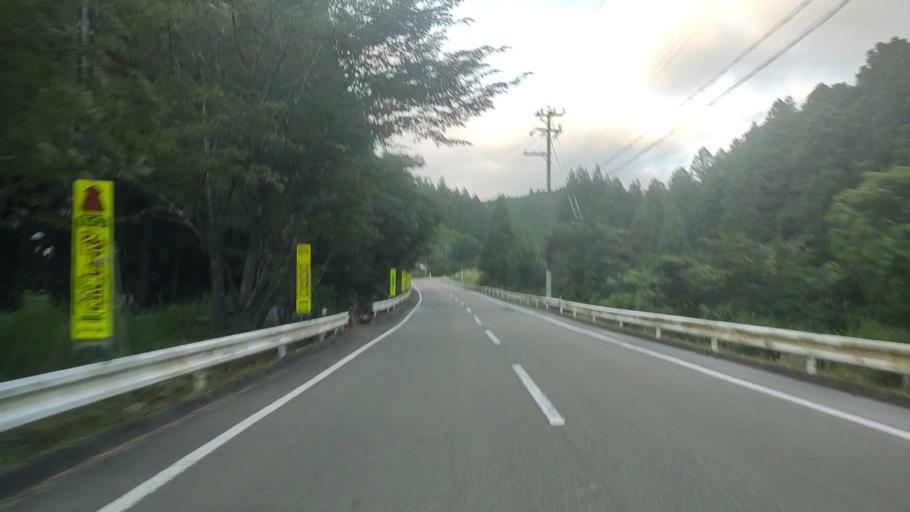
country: JP
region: Wakayama
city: Tanabe
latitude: 33.8302
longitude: 135.6444
